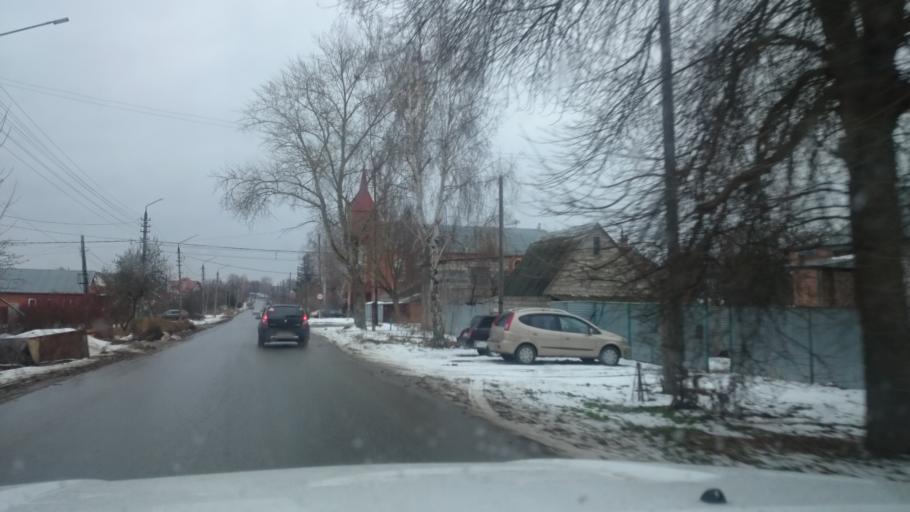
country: RU
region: Tula
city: Tula
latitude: 54.2039
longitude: 37.5587
